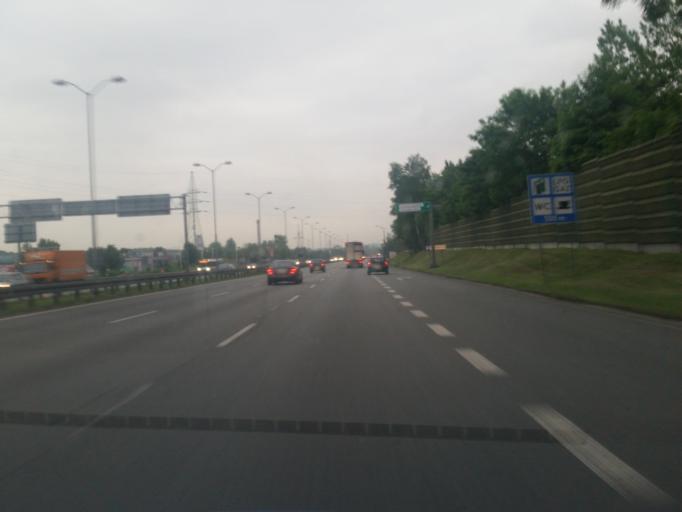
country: PL
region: Silesian Voivodeship
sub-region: Sosnowiec
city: Sosnowiec
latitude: 50.2769
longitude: 19.0773
